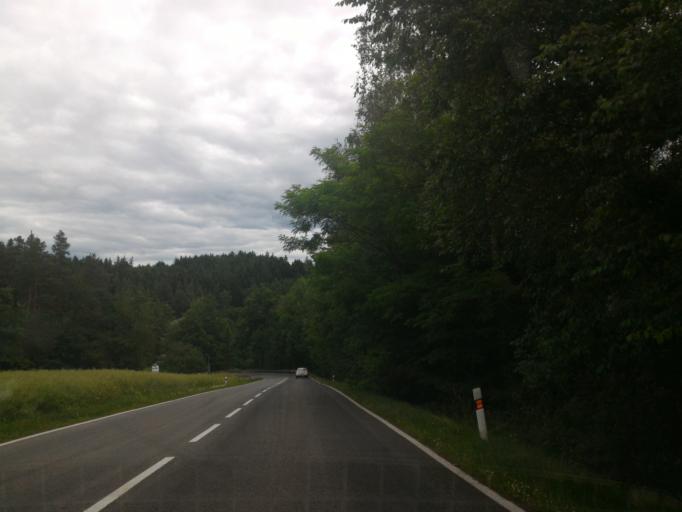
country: CZ
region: Vysocina
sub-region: Okres Pelhrimov
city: Zeliv
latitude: 49.5282
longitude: 15.1713
